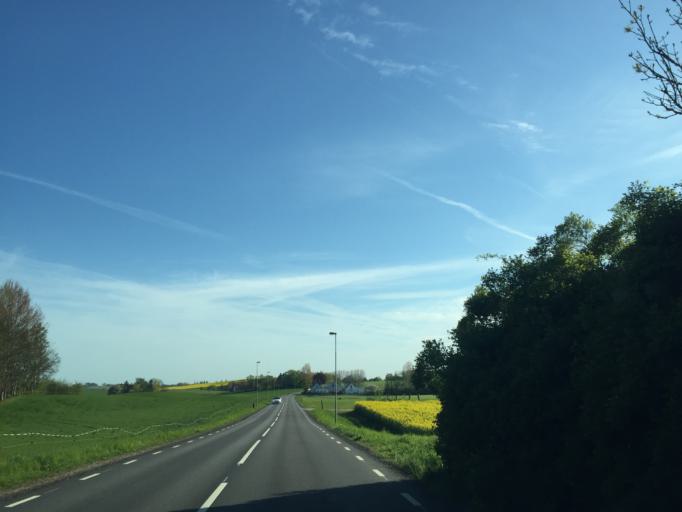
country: SE
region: Skane
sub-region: Malmo
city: Oxie
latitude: 55.5703
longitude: 13.1173
